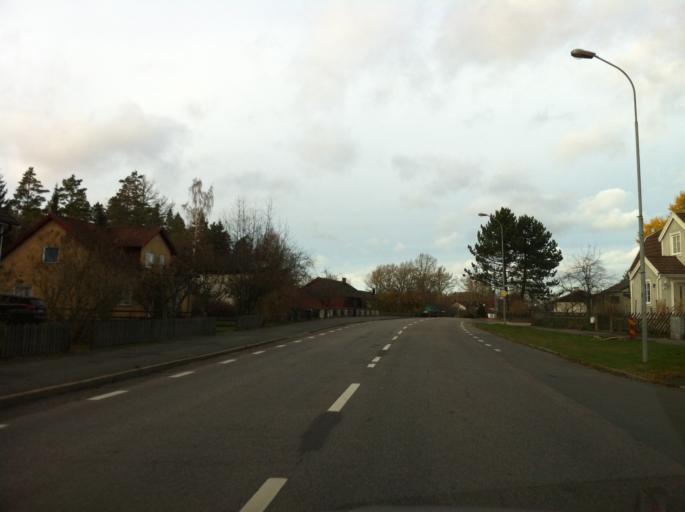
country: SE
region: Kalmar
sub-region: Hultsfreds Kommun
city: Virserum
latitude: 57.1847
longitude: 15.5033
